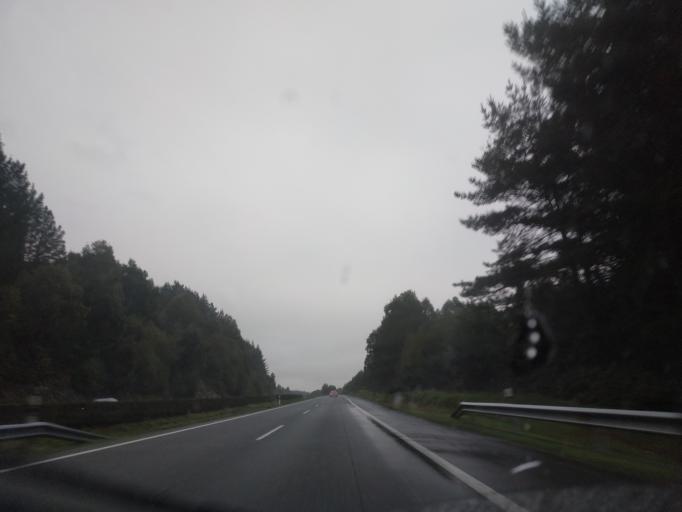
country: ES
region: Galicia
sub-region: Provincia de Lugo
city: Guitiriz
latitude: 43.1810
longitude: -7.8132
